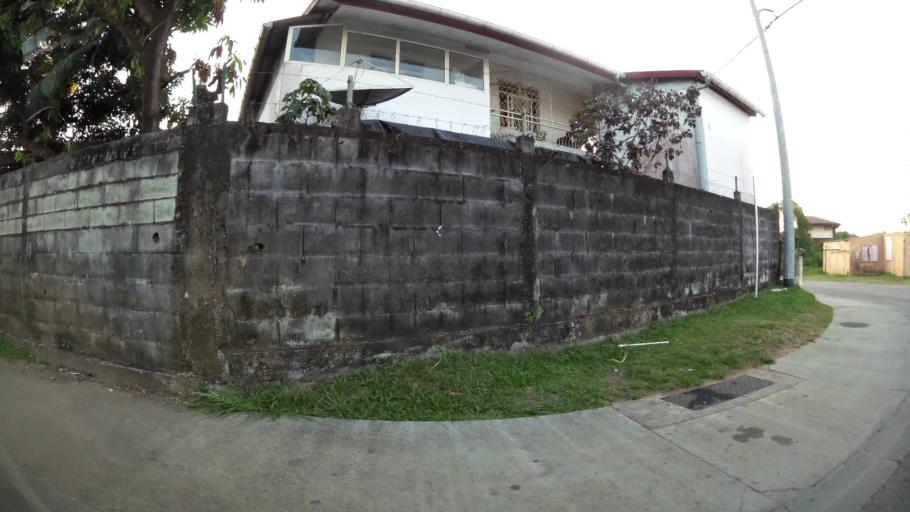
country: GF
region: Guyane
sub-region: Guyane
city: Cayenne
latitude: 4.9279
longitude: -52.3140
